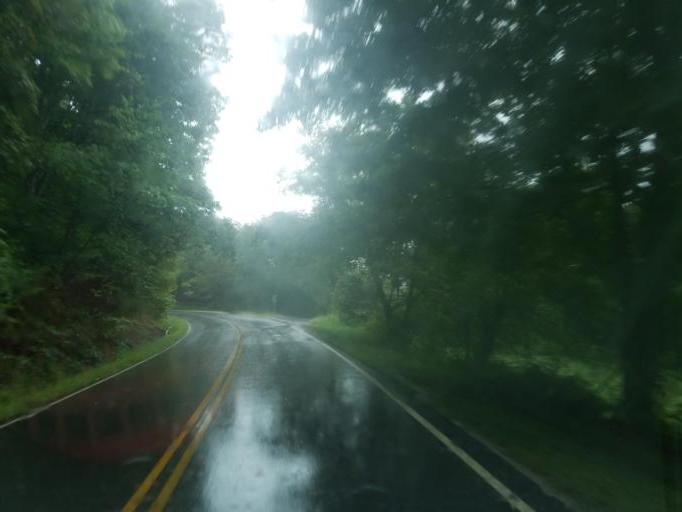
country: US
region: Kentucky
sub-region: Carter County
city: Grayson
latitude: 38.4915
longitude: -82.9903
